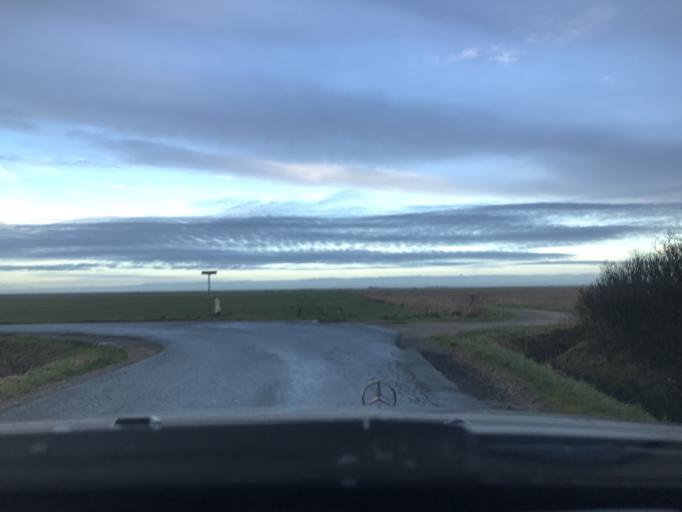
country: DK
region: South Denmark
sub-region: Esbjerg Kommune
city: Ribe
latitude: 55.2998
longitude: 8.6712
